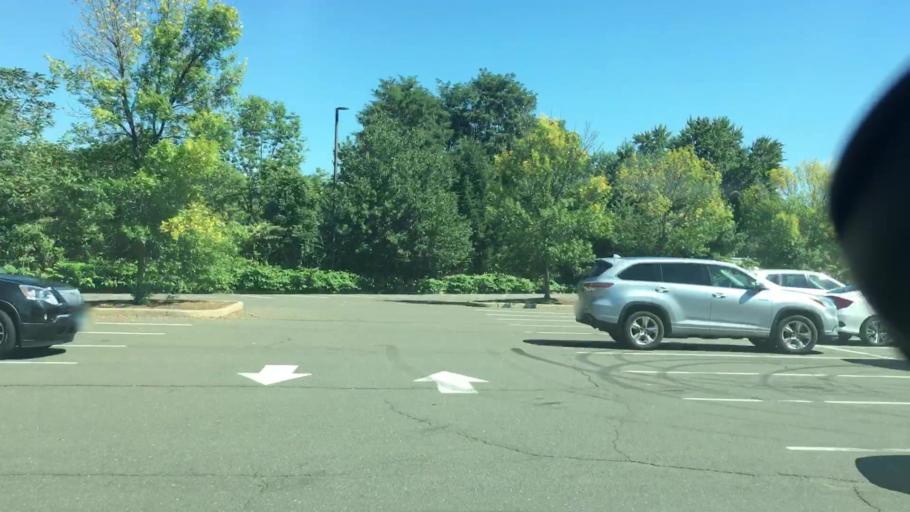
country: US
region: Connecticut
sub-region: Hartford County
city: Manchester
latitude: 41.8144
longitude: -72.5114
